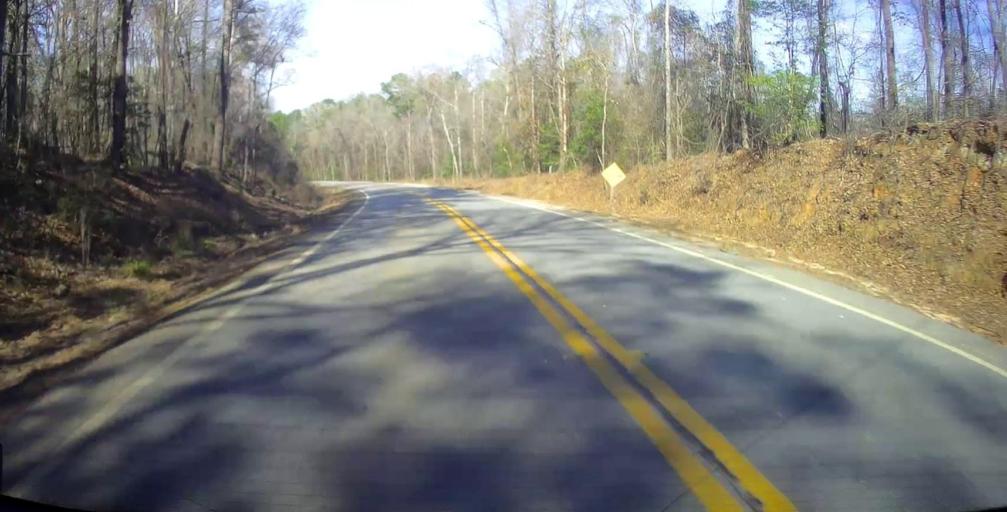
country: US
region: Georgia
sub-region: Wilkinson County
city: Gordon
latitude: 32.8099
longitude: -83.3242
